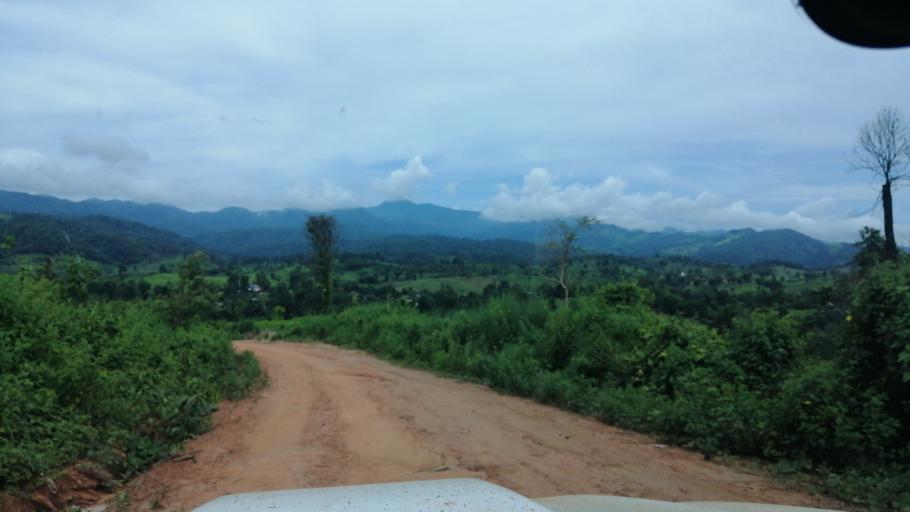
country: TH
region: Loei
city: Na Haeo
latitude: 17.6011
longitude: 101.1217
